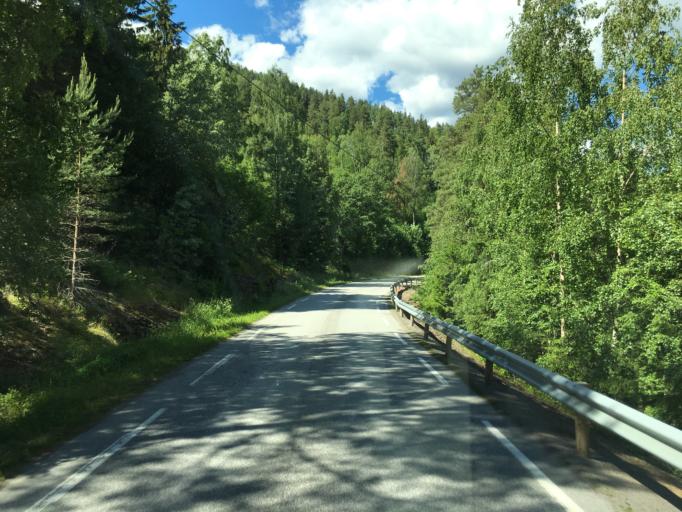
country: NO
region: Oppland
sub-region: Jevnaker
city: Jevnaker
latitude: 60.3518
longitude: 10.3605
